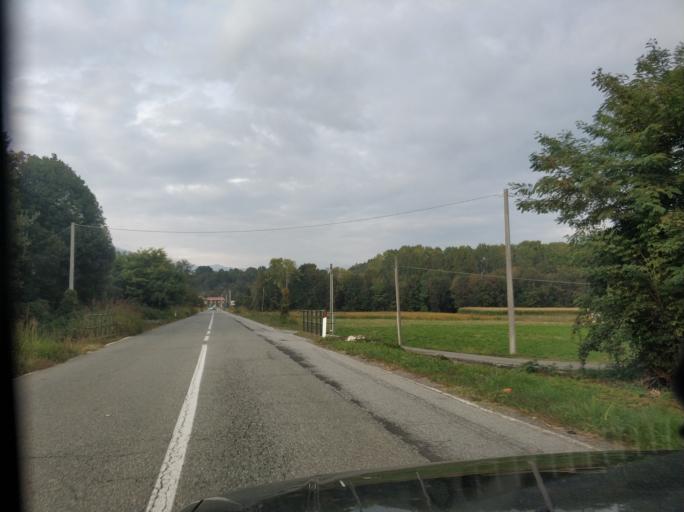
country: IT
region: Piedmont
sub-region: Provincia di Torino
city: Grosso
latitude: 45.2556
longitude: 7.5624
